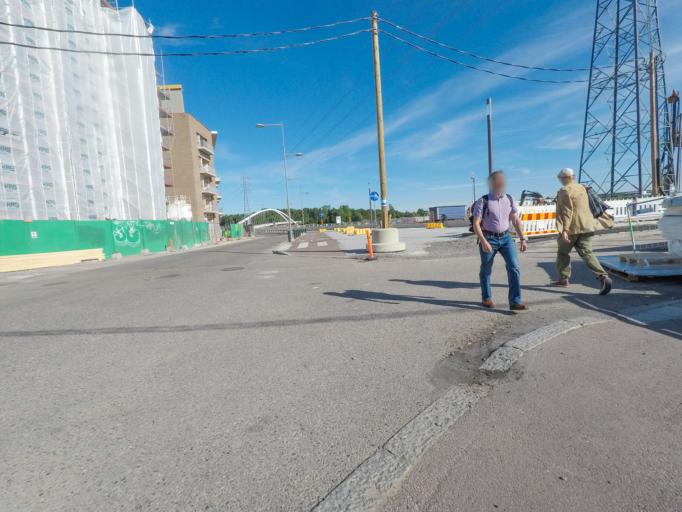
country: FI
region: Uusimaa
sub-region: Helsinki
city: Helsinki
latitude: 60.1834
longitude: 24.9766
